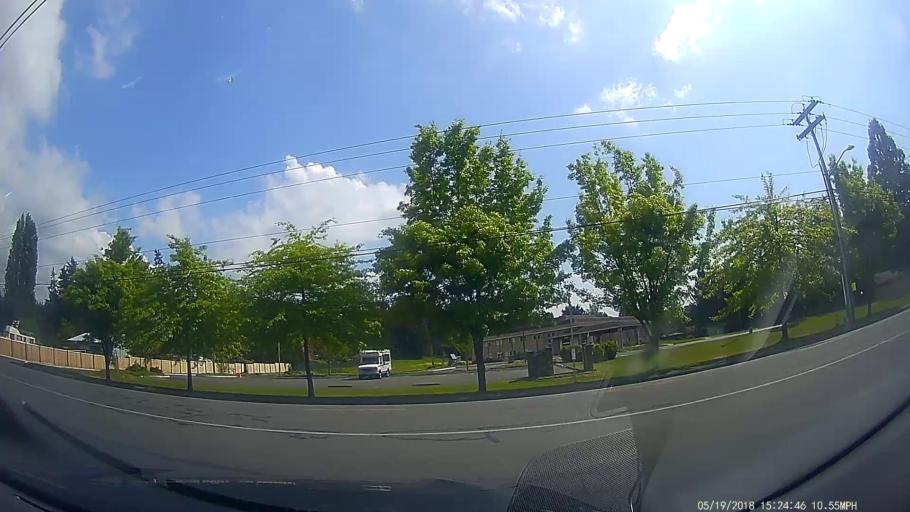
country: US
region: Washington
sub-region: Skagit County
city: Mount Vernon
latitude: 48.4317
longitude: -122.3058
